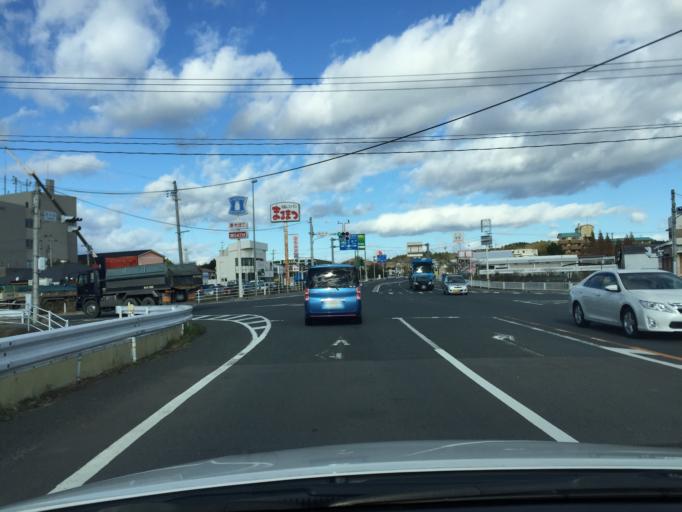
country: JP
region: Fukushima
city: Namie
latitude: 37.4936
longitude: 141.0023
